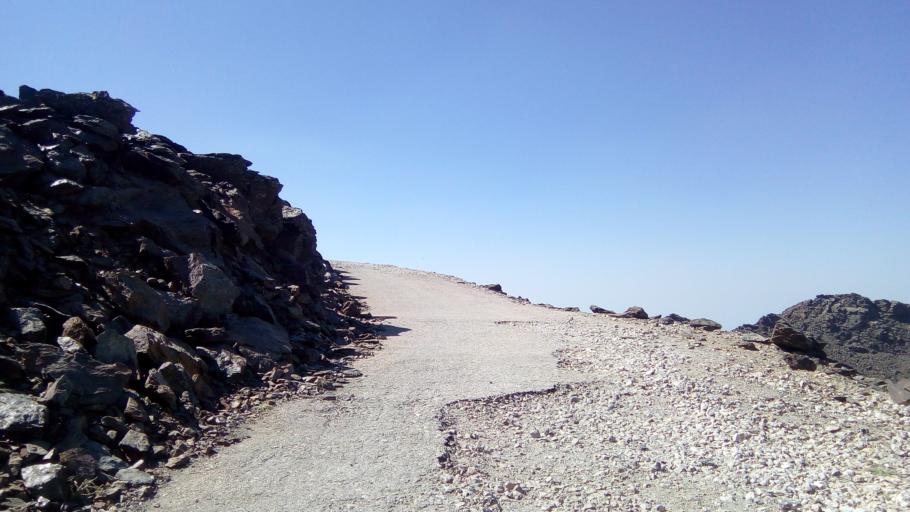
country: ES
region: Andalusia
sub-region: Provincia de Granada
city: Capileira
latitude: 37.0518
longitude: -3.3716
